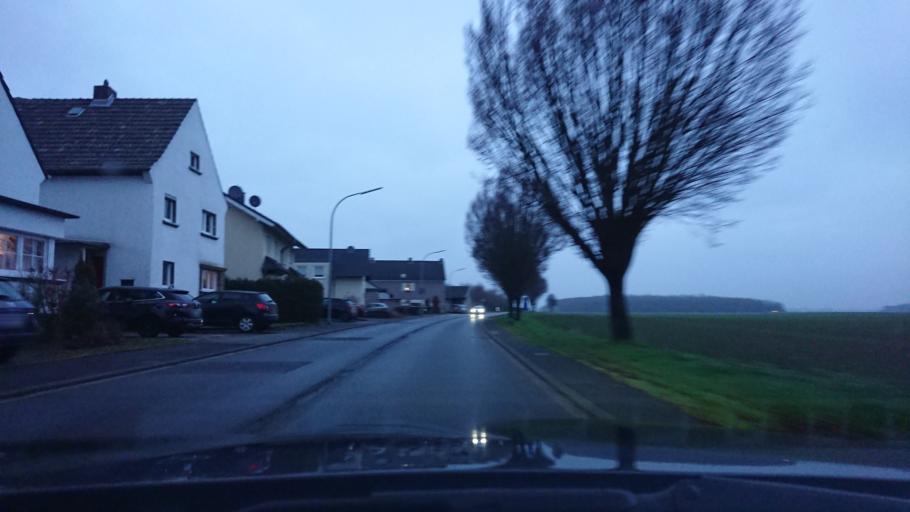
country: DE
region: North Rhine-Westphalia
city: Niederkassel
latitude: 50.8387
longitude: 7.0330
